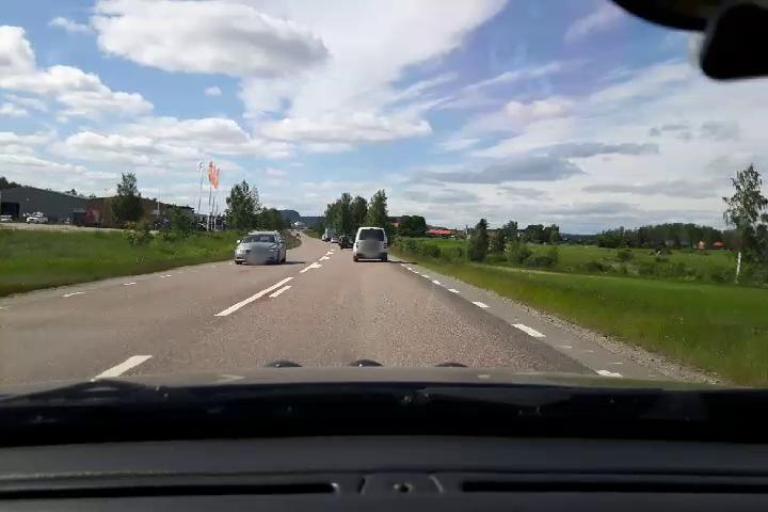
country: SE
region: Gaevleborg
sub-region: Bollnas Kommun
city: Bollnas
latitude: 61.3328
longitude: 16.4075
